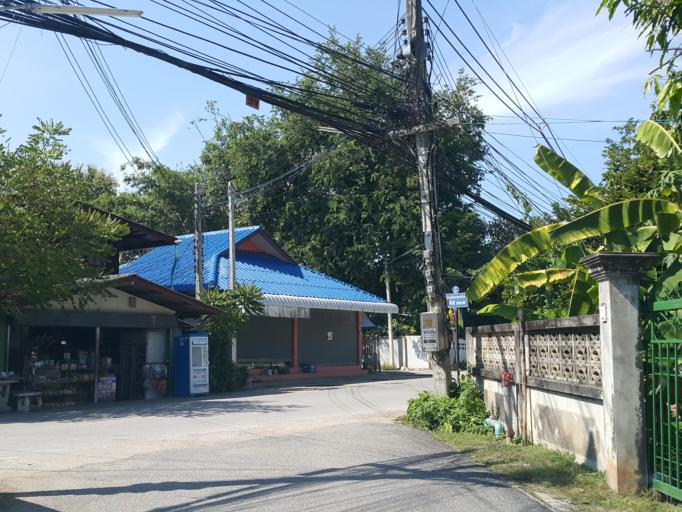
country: TH
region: Chiang Mai
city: Saraphi
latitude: 18.7667
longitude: 99.0555
